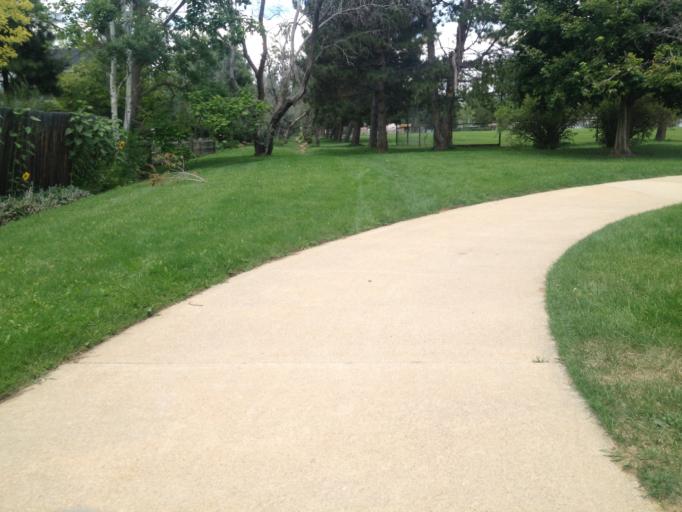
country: US
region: Colorado
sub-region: Boulder County
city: Louisville
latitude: 39.9743
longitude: -105.1402
